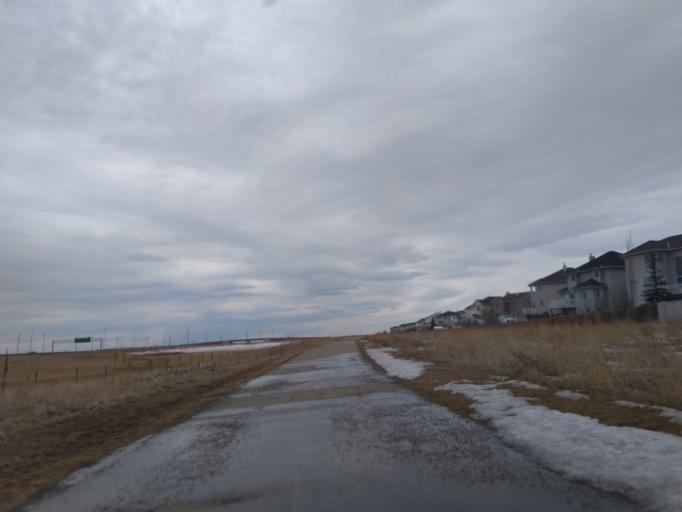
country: CA
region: Alberta
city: Chestermere
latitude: 51.1081
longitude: -113.9225
